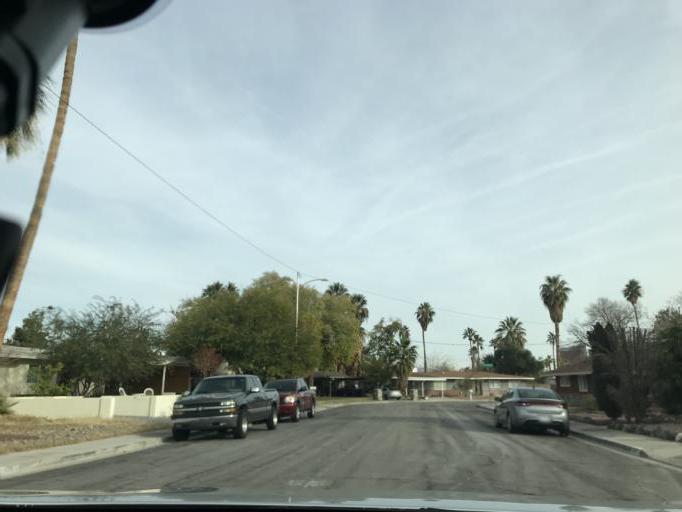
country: US
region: Nevada
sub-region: Clark County
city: Las Vegas
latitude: 36.1723
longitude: -115.1712
